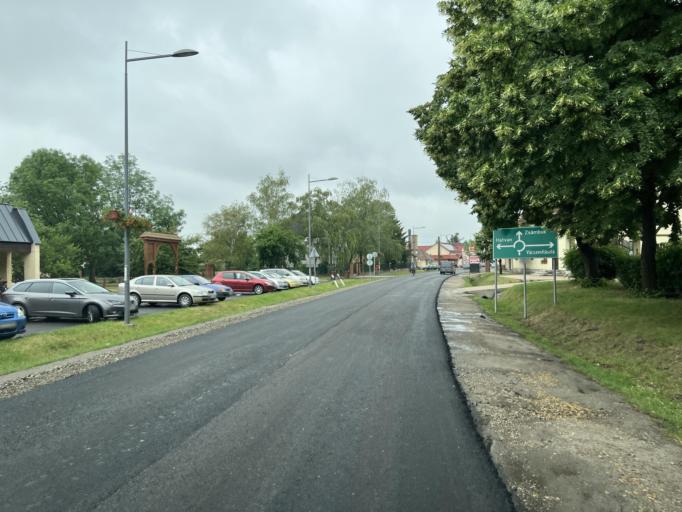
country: HU
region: Pest
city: Tura
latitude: 47.6113
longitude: 19.6003
